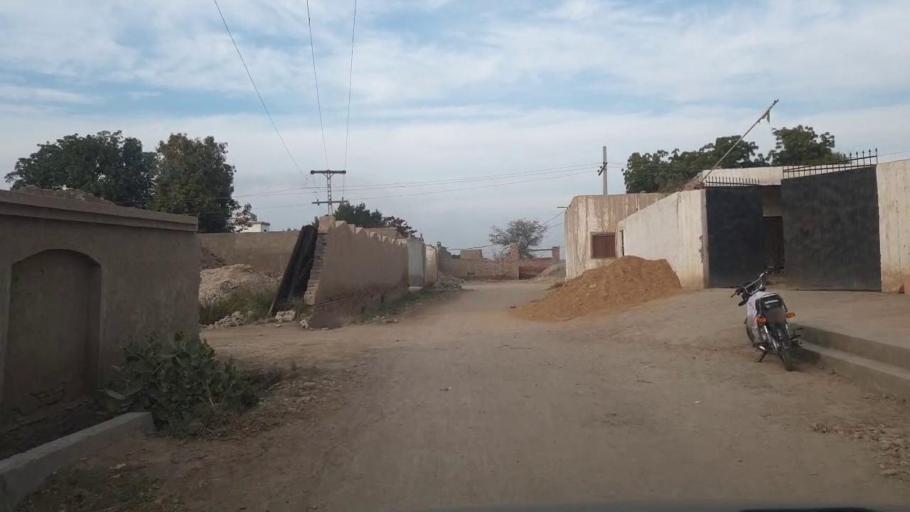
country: PK
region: Sindh
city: Shahpur Chakar
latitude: 26.1386
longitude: 68.6082
